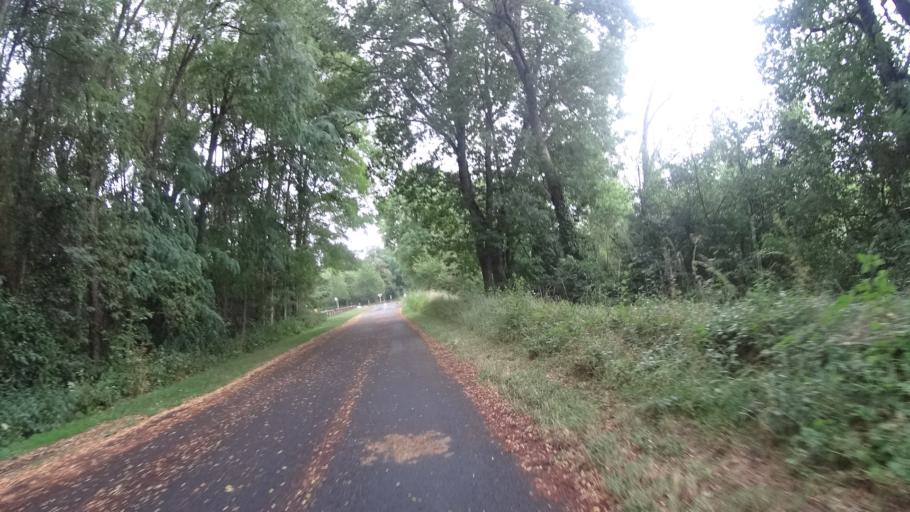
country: FR
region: Centre
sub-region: Departement du Loir-et-Cher
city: La Chaussee-Saint-Victor
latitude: 47.6100
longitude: 1.3713
